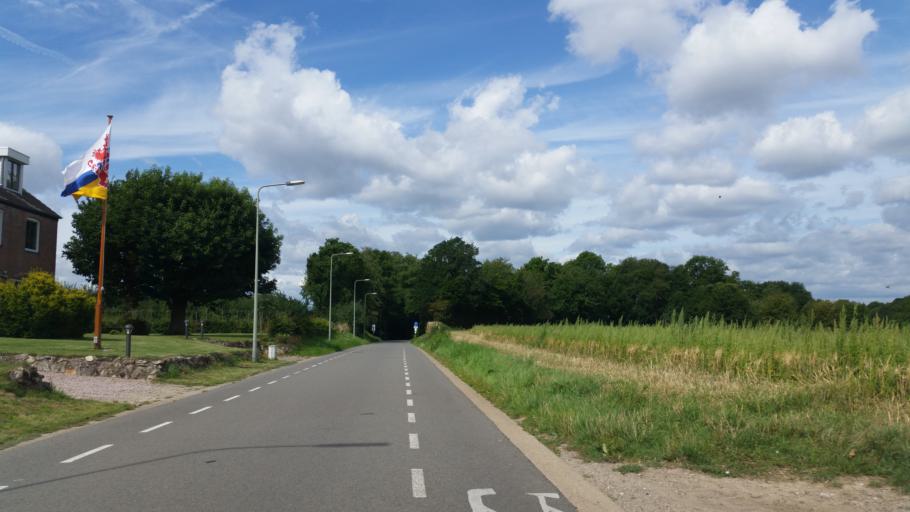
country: NL
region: Limburg
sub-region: Gemeente Maastricht
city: Heer
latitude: 50.8473
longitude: 5.7542
